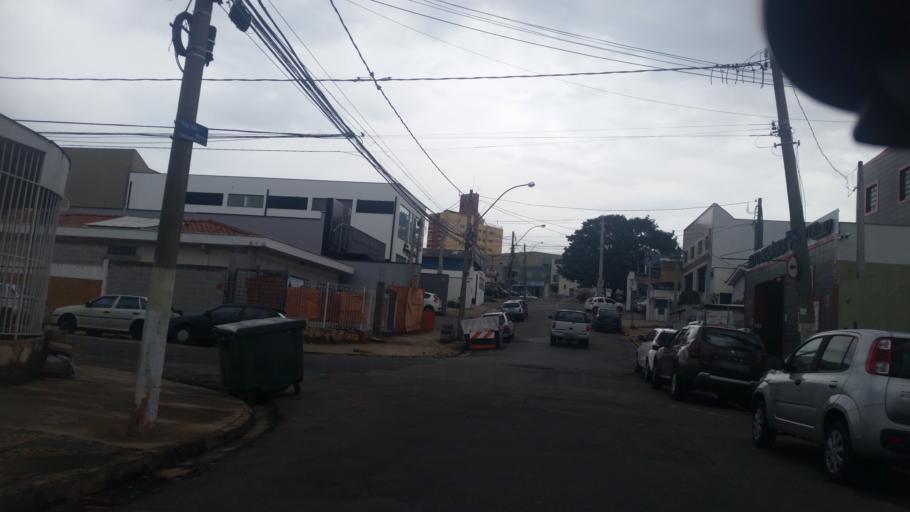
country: BR
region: Sao Paulo
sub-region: Campinas
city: Campinas
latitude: -22.8827
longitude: -47.0645
